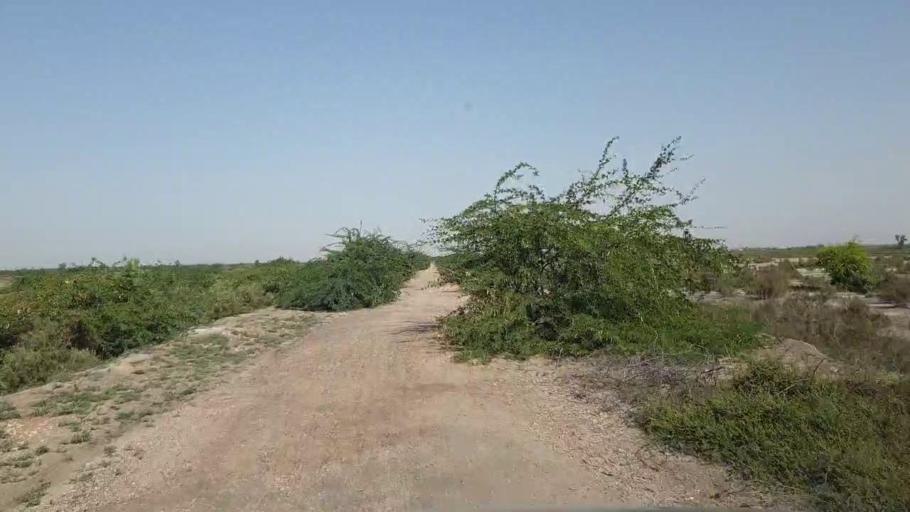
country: PK
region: Sindh
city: Tando Bago
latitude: 24.7143
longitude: 69.0724
